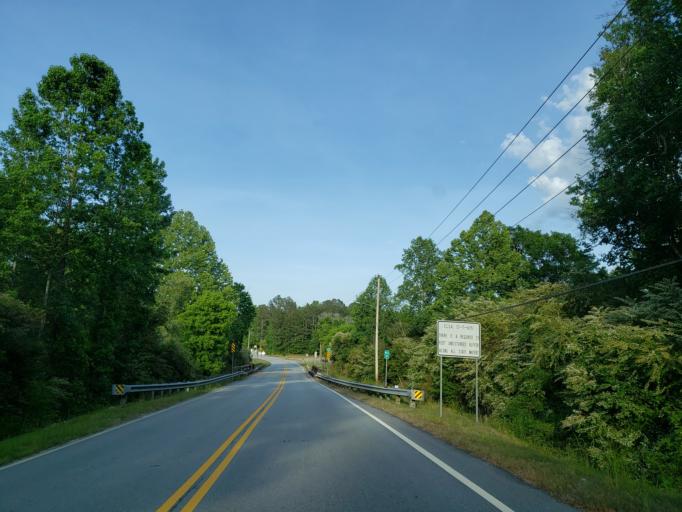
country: US
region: Georgia
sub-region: Carroll County
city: Mount Zion
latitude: 33.6367
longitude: -85.1992
